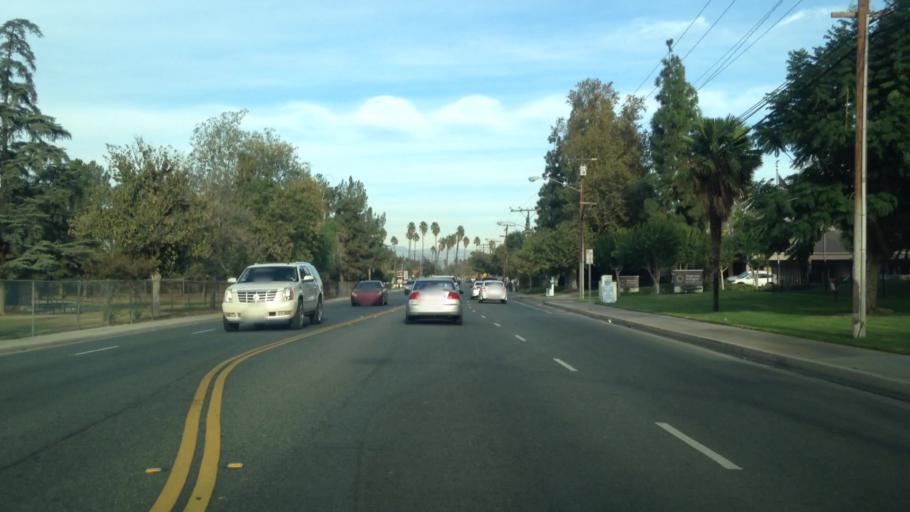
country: US
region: California
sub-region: Riverside County
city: Riverside
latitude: 33.9437
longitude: -117.4216
